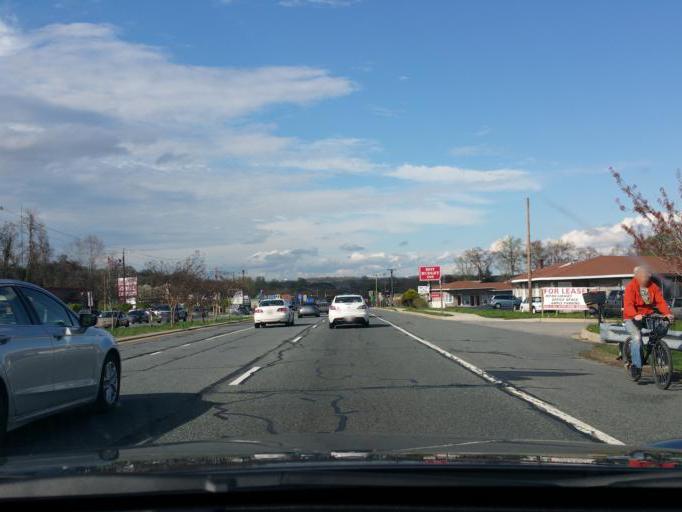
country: US
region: Maryland
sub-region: Harford County
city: Havre de Grace
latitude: 39.5501
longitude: -76.1037
